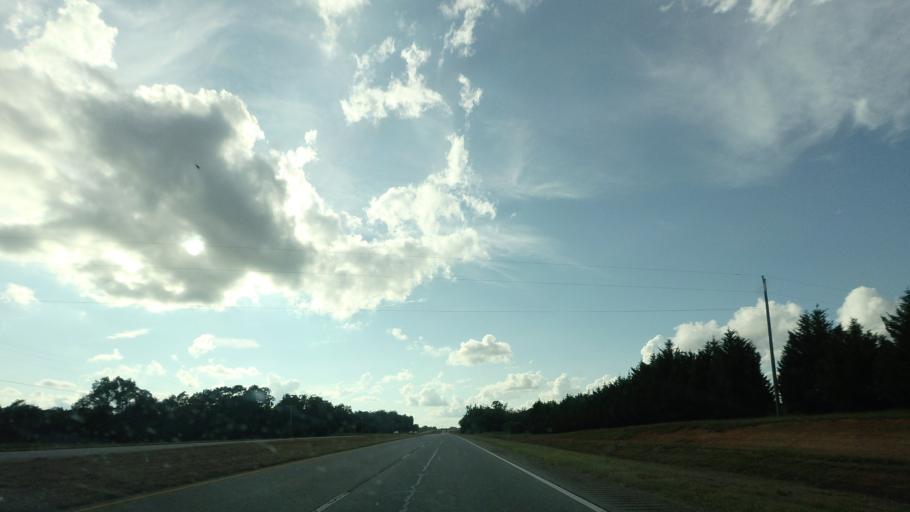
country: US
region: Georgia
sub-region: Pulaski County
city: Hawkinsville
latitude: 32.3133
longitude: -83.5249
